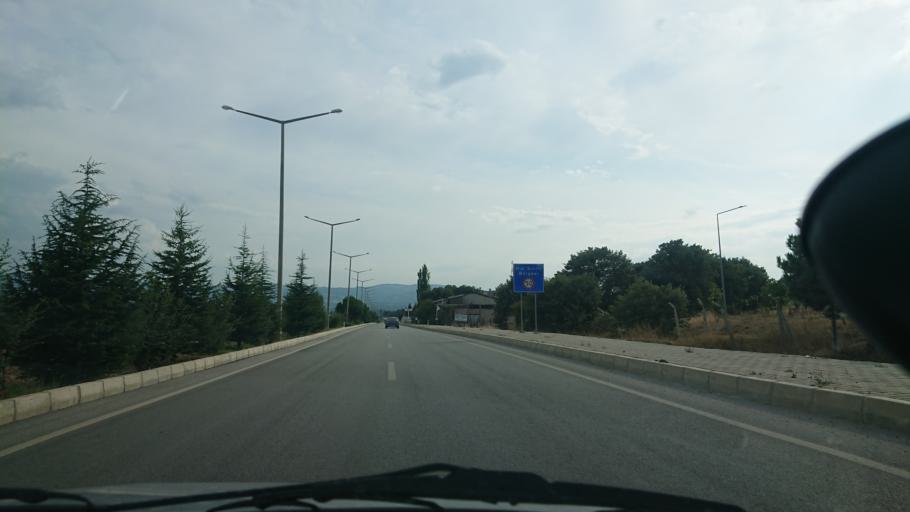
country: TR
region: Kuetahya
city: Gediz
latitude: 39.0054
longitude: 29.4054
